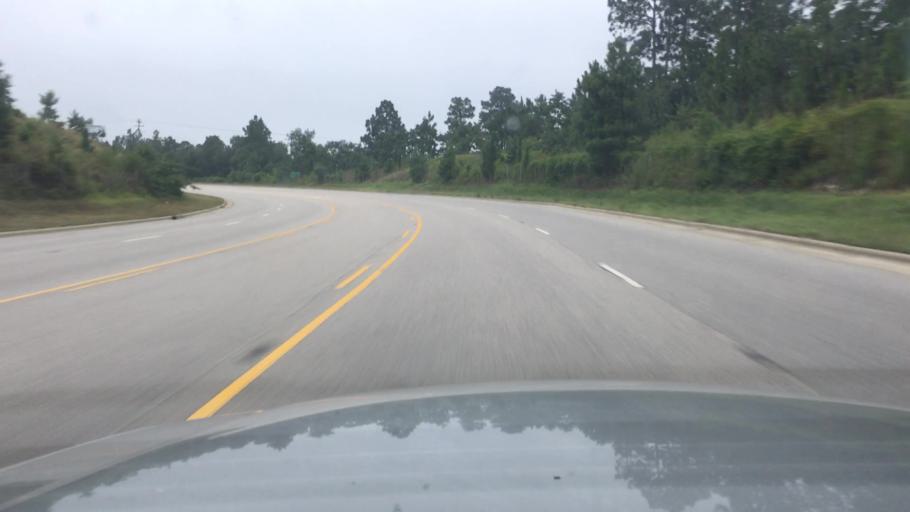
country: US
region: North Carolina
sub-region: Cumberland County
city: Fayetteville
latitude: 35.0138
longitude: -78.8890
